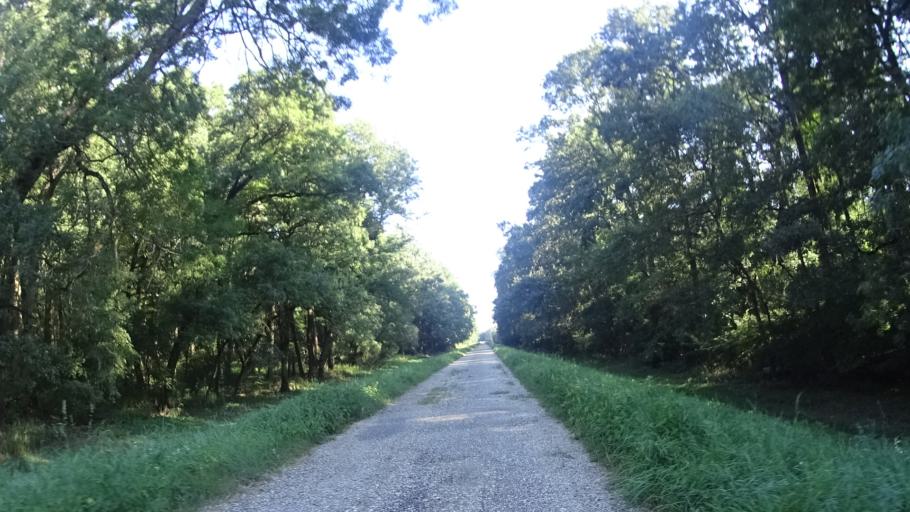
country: AT
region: Lower Austria
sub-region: Politischer Bezirk Mistelbach
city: Rabensburg
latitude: 48.6358
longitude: 16.9781
